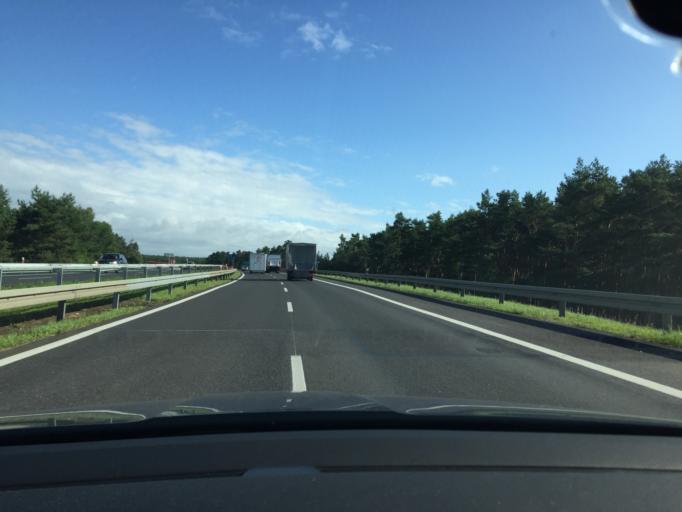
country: PL
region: West Pomeranian Voivodeship
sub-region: Powiat goleniowski
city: Goleniow
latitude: 53.5290
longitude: 14.8115
